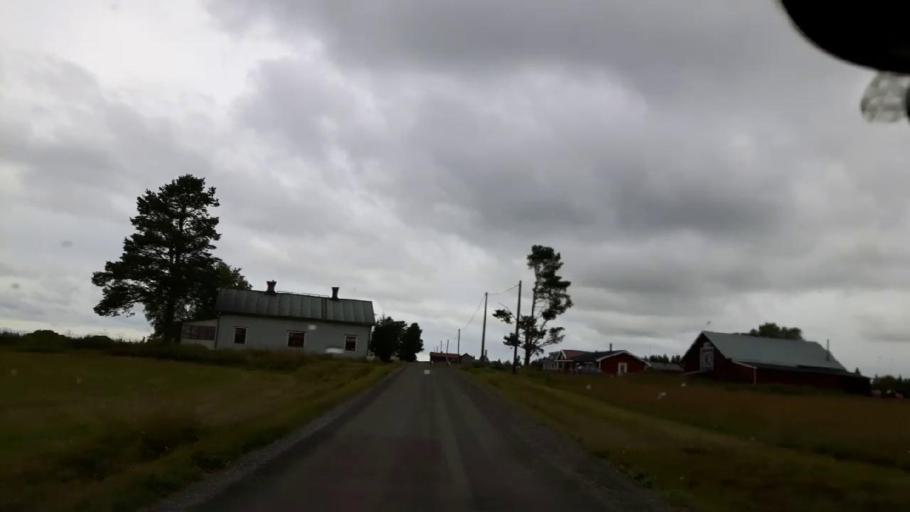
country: SE
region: Jaemtland
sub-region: OEstersunds Kommun
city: Ostersund
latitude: 63.0522
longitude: 14.5668
